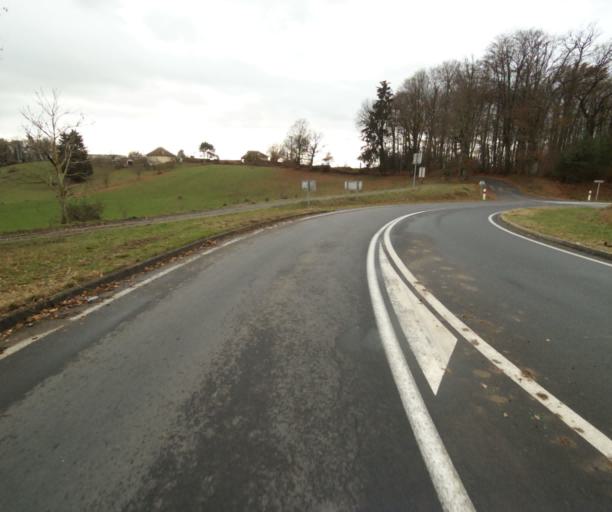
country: FR
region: Limousin
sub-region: Departement de la Correze
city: Saint-Mexant
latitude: 45.2790
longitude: 1.6196
